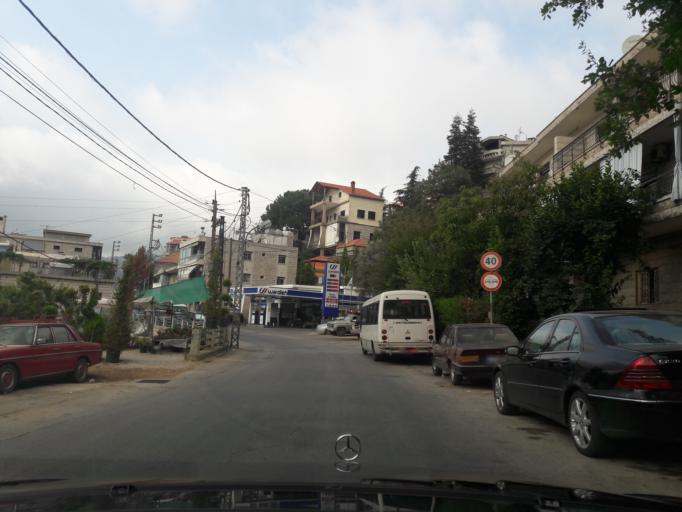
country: LB
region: Mont-Liban
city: Djounie
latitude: 33.9278
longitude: 35.7415
